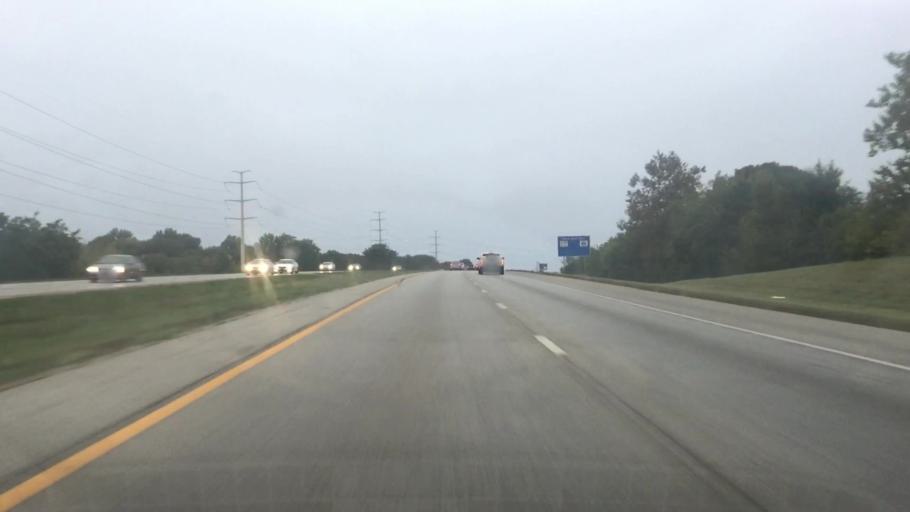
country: US
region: Kansas
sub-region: Johnson County
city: Lenexa
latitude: 38.9067
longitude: -94.6895
